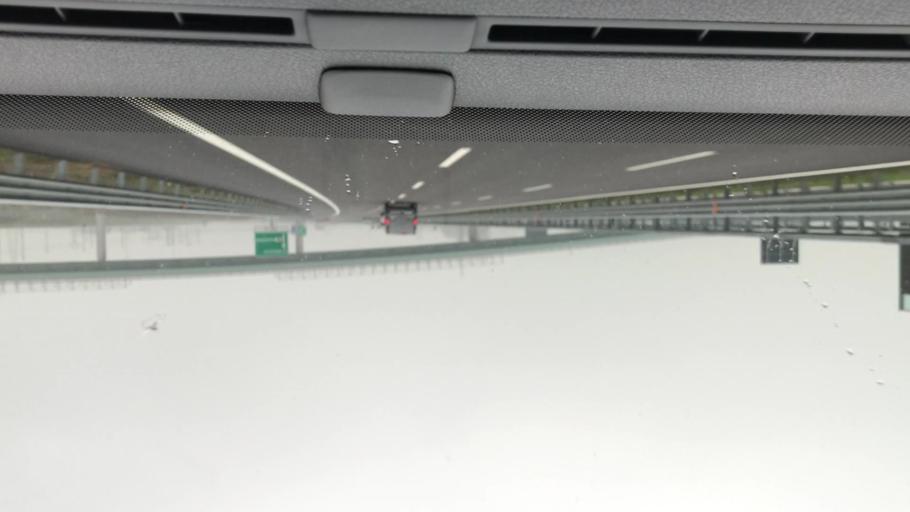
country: IT
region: Lombardy
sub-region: Provincia di Bergamo
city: Fornovo San Giovanni
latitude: 45.5102
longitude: 9.6804
